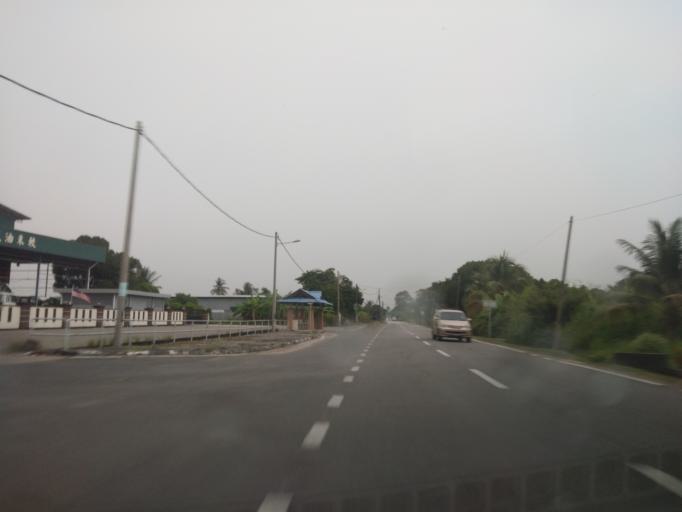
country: MY
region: Penang
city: Permatang Kuching
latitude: 5.4950
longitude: 100.3977
